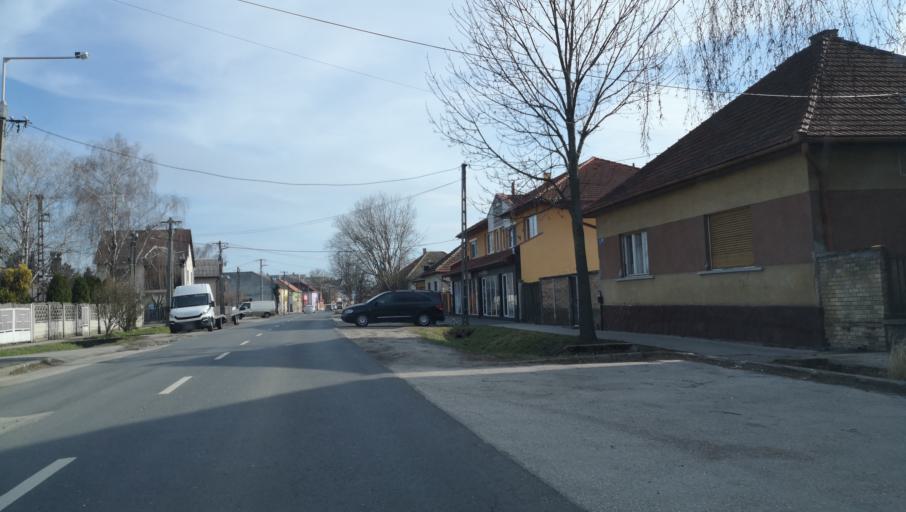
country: HU
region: Pest
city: Monor
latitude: 47.3549
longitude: 19.4425
